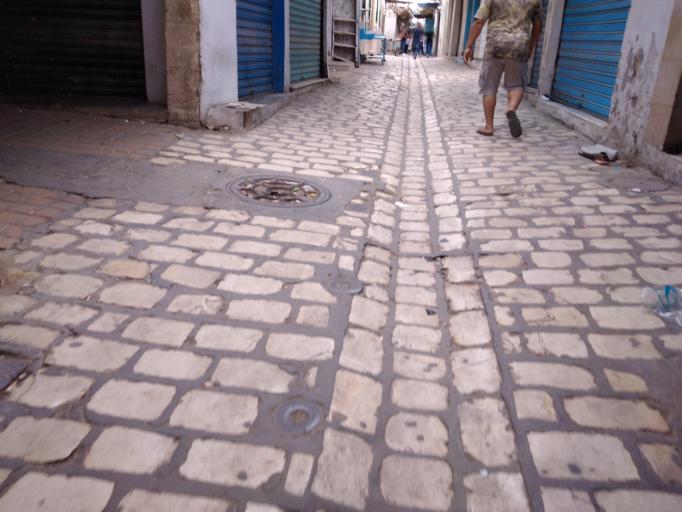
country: TN
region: Safaqis
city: Sfax
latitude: 34.7366
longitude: 10.7610
